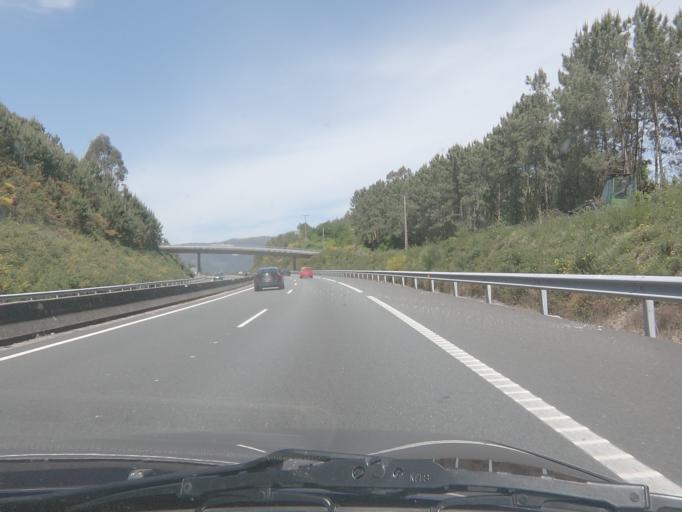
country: ES
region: Galicia
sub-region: Provincia de Pontevedra
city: Portas
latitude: 42.5700
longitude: -8.6707
